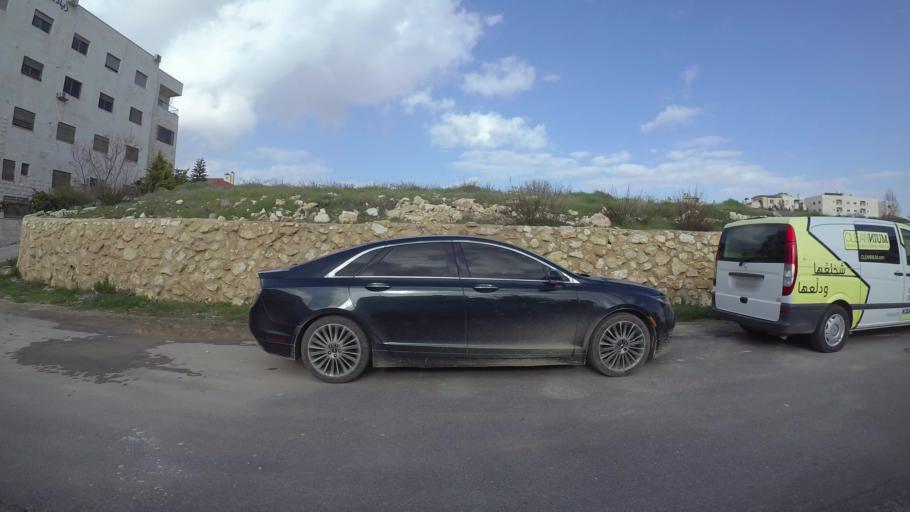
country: JO
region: Amman
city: Al Jubayhah
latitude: 31.9837
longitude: 35.8510
